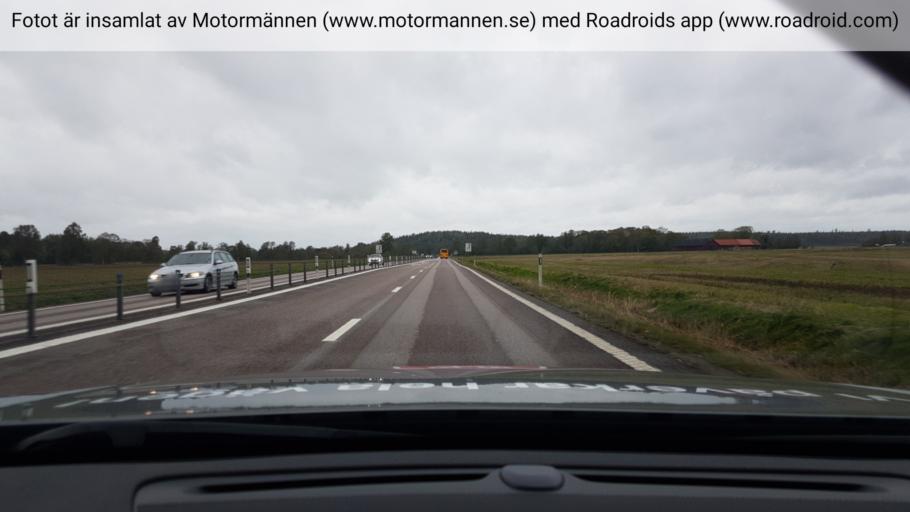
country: SE
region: Vaermland
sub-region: Kristinehamns Kommun
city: Kristinehamn
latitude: 59.3742
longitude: 13.9850
